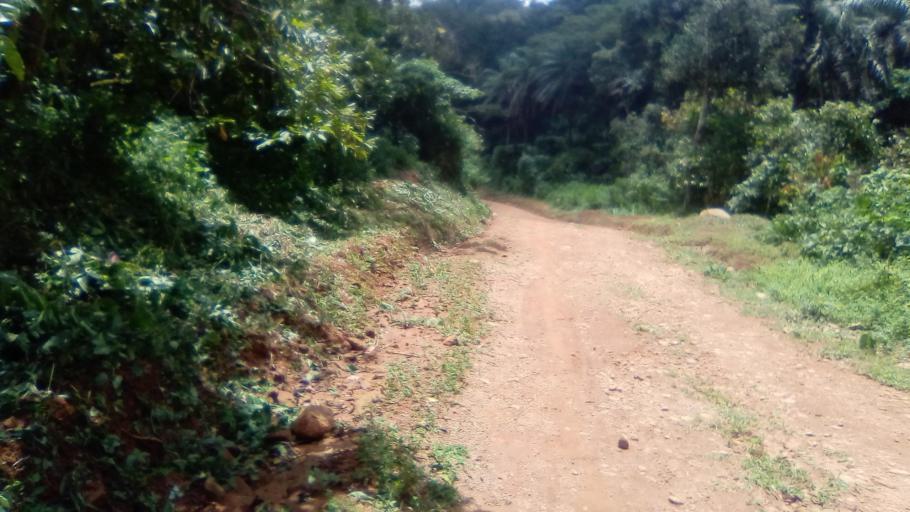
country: SL
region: Eastern Province
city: Giehun
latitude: 8.5029
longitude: -10.9060
